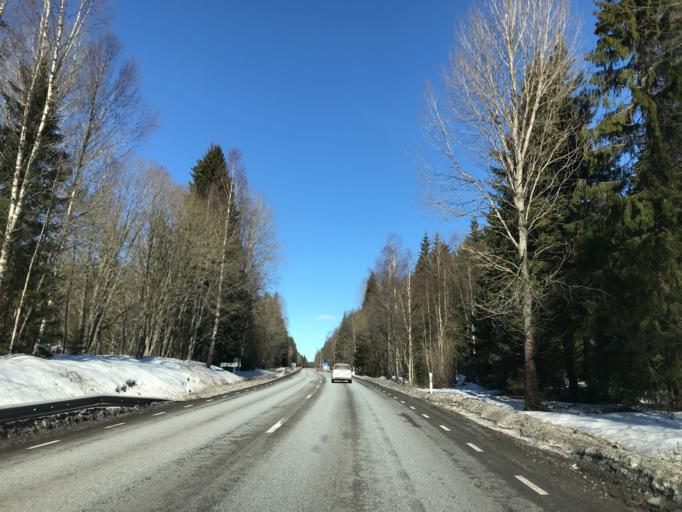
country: SE
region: Vaermland
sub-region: Filipstads Kommun
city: Filipstad
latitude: 59.7618
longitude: 14.2582
